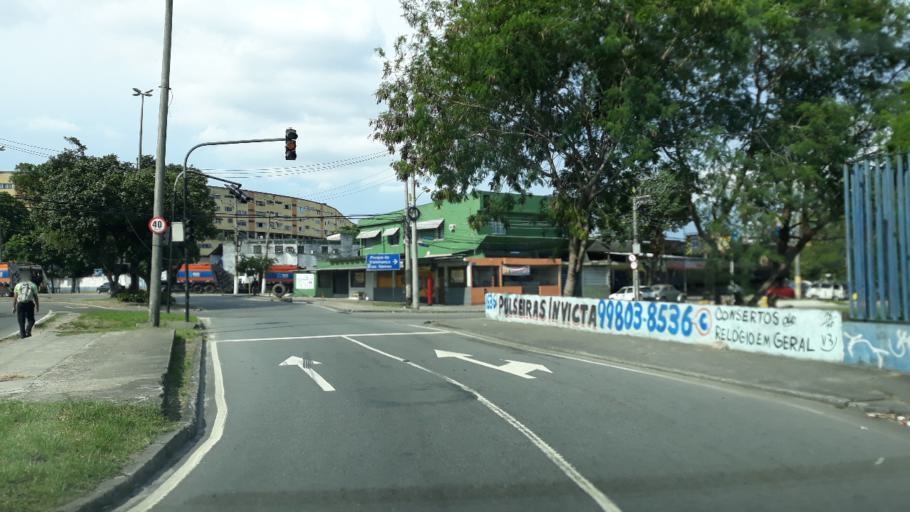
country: BR
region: Rio de Janeiro
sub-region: Sao Joao De Meriti
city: Sao Joao de Meriti
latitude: -22.8521
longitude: -43.3840
